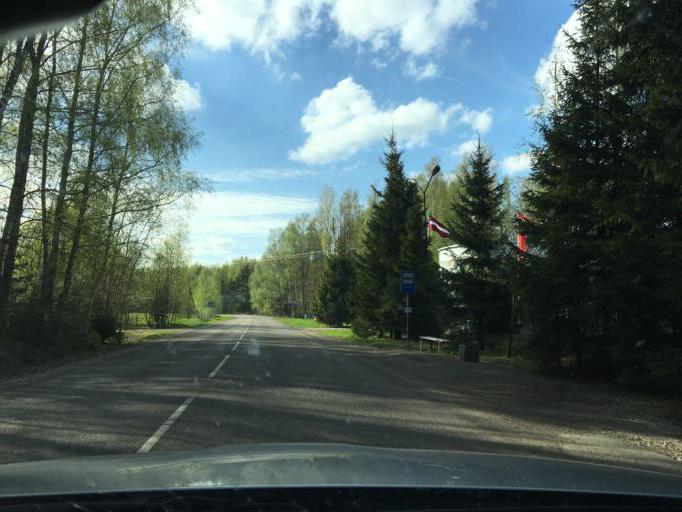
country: LV
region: Ozolnieku
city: Ozolnieki
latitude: 56.6869
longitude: 23.8309
